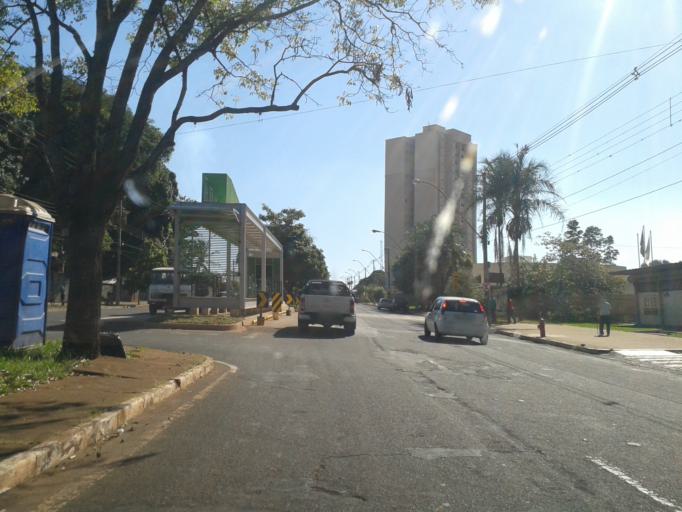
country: BR
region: Minas Gerais
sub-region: Uberaba
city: Uberaba
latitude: -19.7469
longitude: -47.9488
